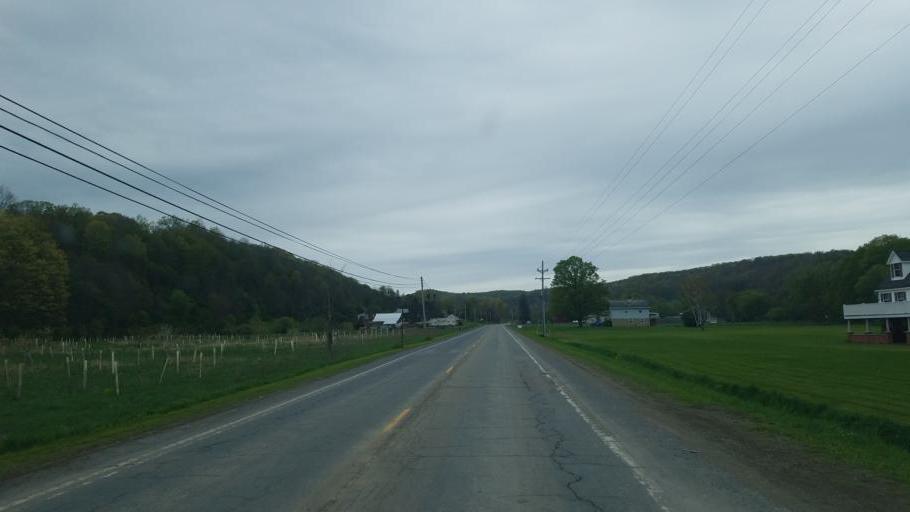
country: US
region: Pennsylvania
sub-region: Tioga County
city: Westfield
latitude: 41.9235
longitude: -77.6256
